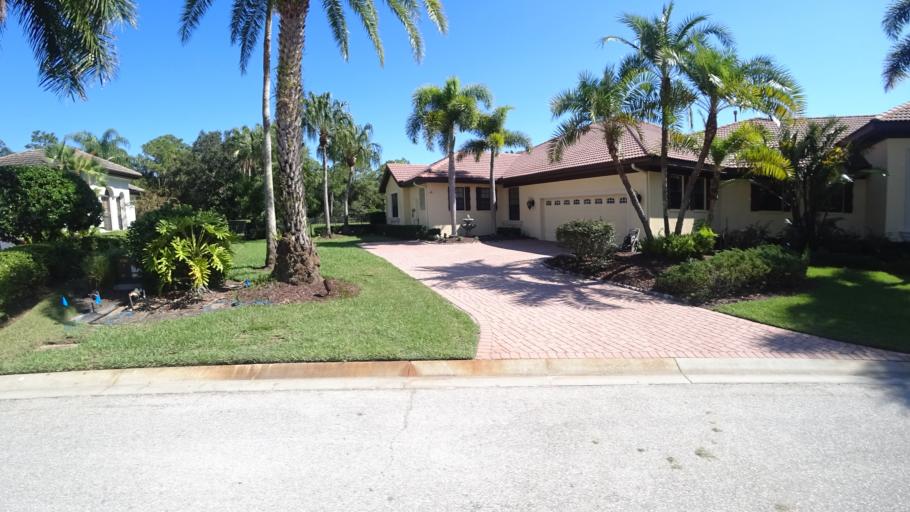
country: US
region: Florida
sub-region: Sarasota County
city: The Meadows
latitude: 27.4092
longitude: -82.4085
